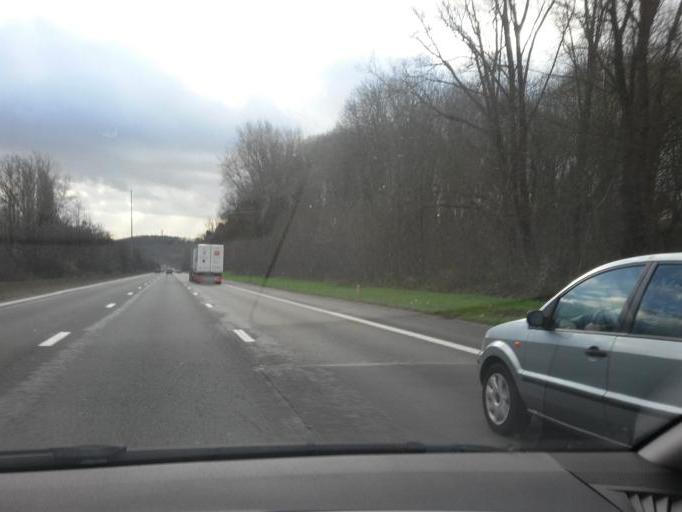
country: BE
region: Flanders
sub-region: Provincie Vlaams-Brabant
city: Hoeilaart
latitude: 50.7760
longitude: 4.4998
